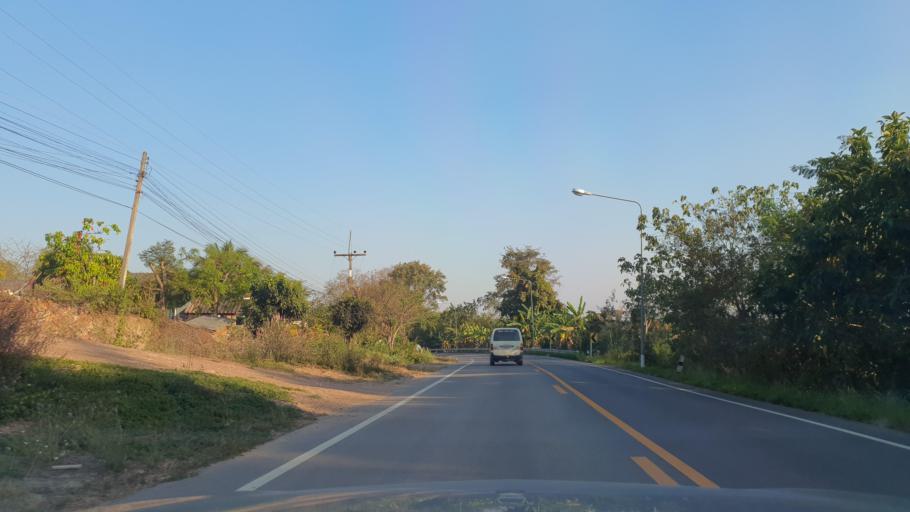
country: TH
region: Chiang Rai
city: Mae Lao
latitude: 19.8331
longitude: 99.6862
